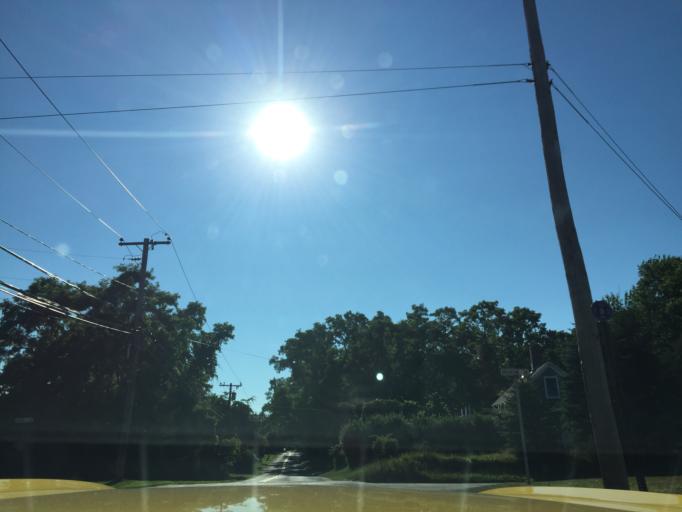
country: US
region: New York
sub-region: Suffolk County
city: Southold
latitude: 41.0427
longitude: -72.4041
